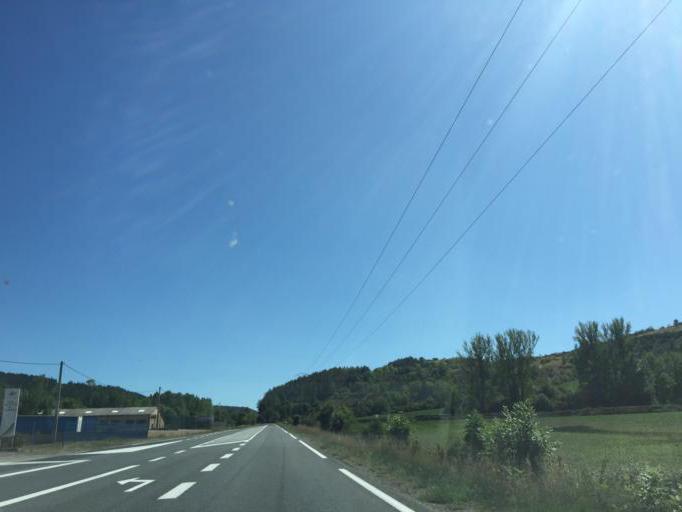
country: FR
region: Midi-Pyrenees
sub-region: Departement de l'Aveyron
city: Saint-Georges-de-Luzencon
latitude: 43.9900
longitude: 2.9672
